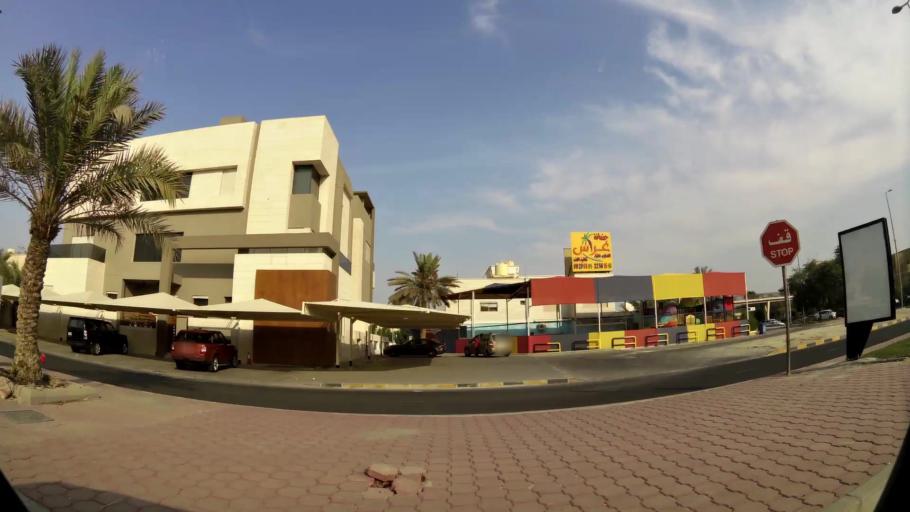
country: KW
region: Muhafazat Hawalli
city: Hawalli
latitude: 29.3218
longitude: 47.9982
